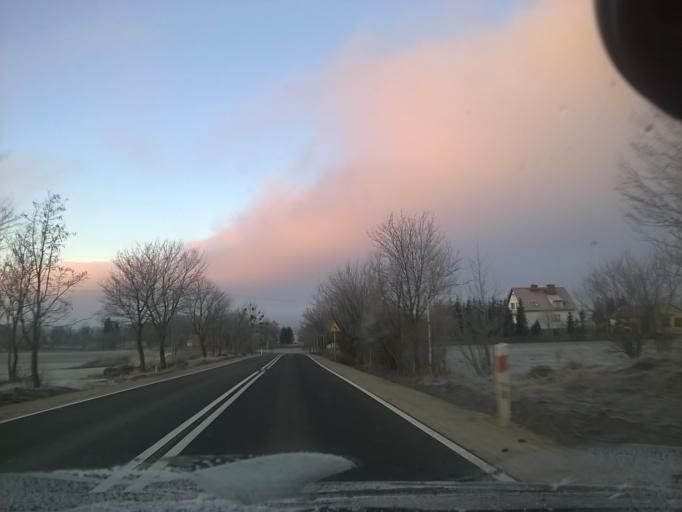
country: PL
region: Warmian-Masurian Voivodeship
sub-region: Powiat ketrzynski
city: Ketrzyn
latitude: 54.0589
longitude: 21.3426
